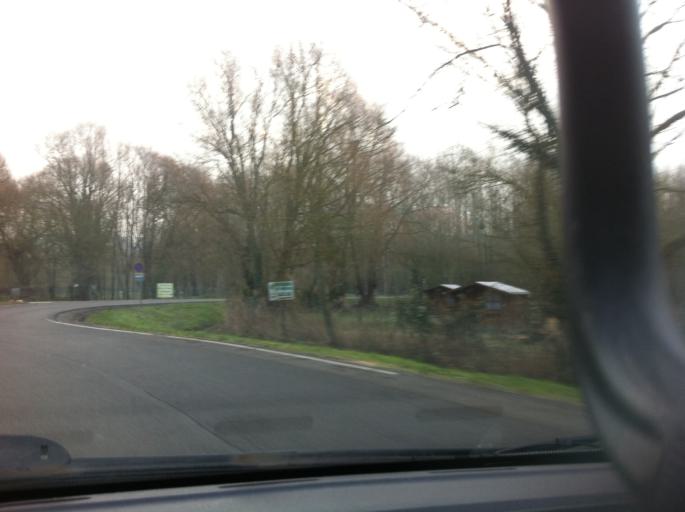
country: FR
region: Ile-de-France
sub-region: Departement de l'Essonne
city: Etampes
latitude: 48.4261
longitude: 2.1532
